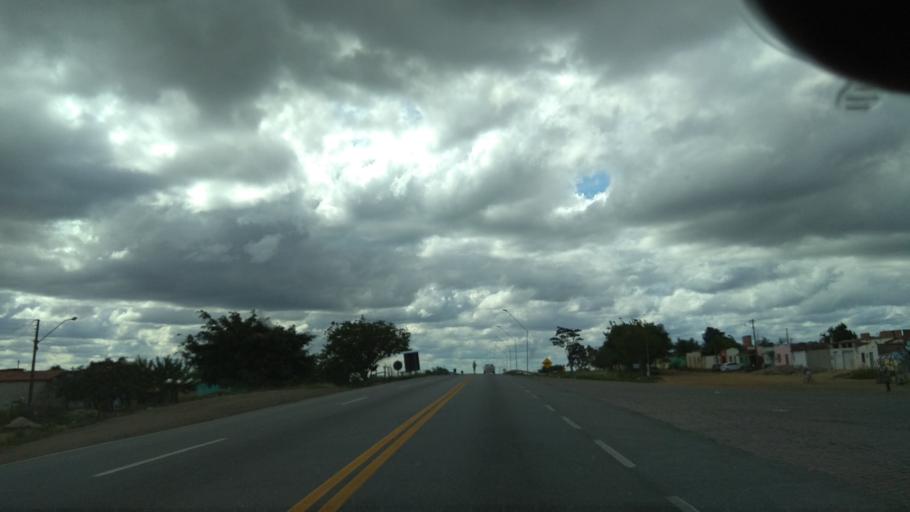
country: BR
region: Bahia
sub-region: Santa Ines
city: Santa Ines
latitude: -13.0725
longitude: -39.9611
